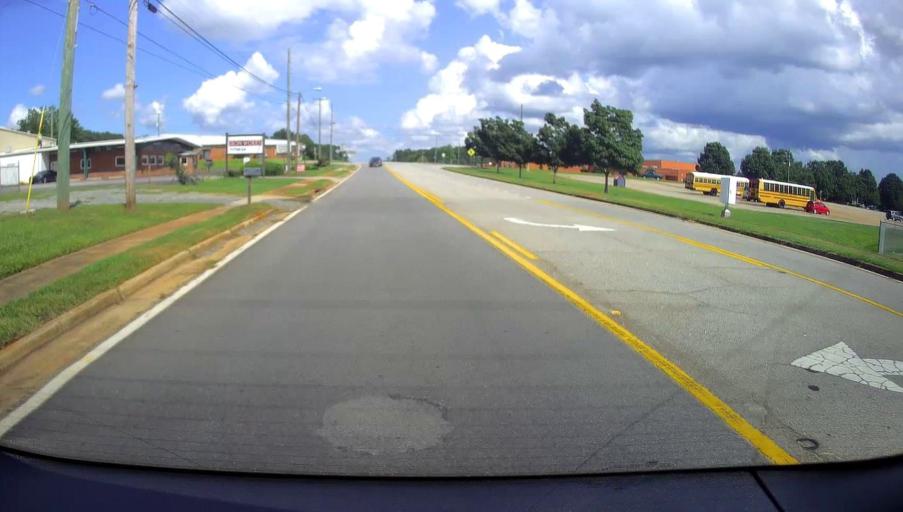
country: US
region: Georgia
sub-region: Upson County
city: Thomaston
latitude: 32.8880
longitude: -84.3159
